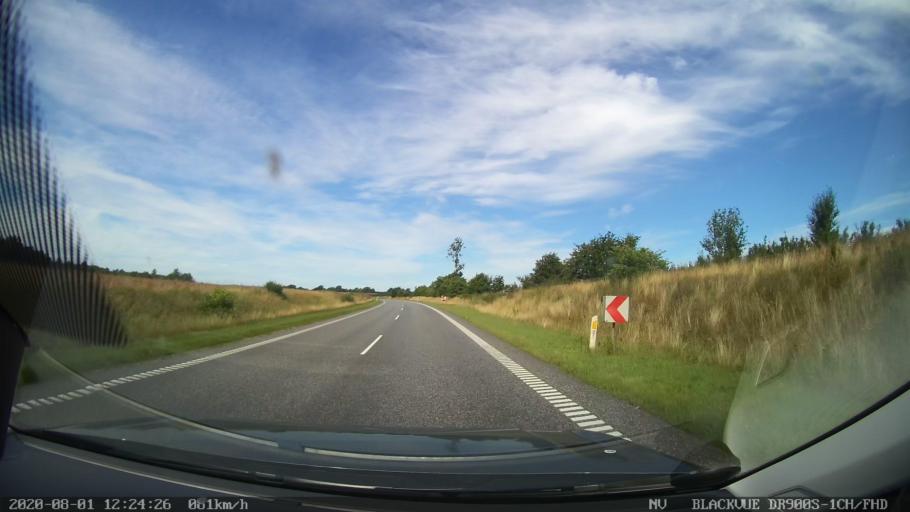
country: DK
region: Central Jutland
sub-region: Viborg Kommune
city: Stoholm
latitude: 56.4051
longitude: 9.1282
